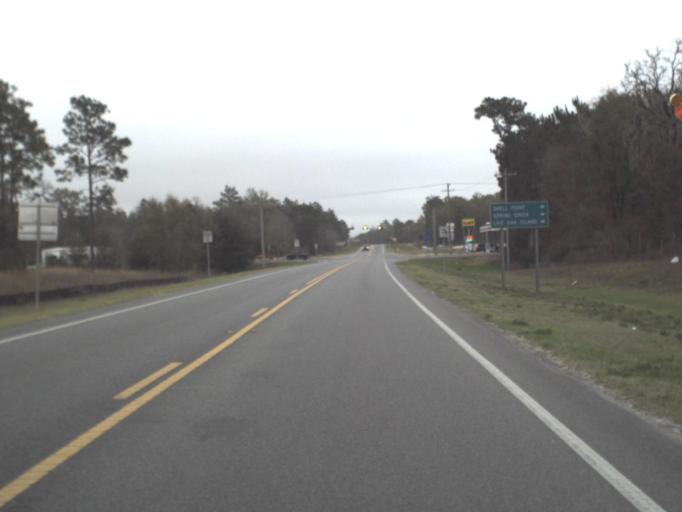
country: US
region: Florida
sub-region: Wakulla County
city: Crawfordville
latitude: 30.1404
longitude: -84.3158
